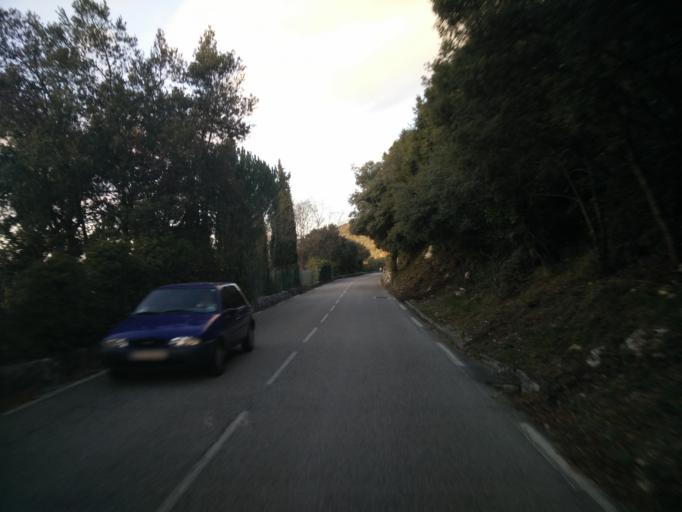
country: FR
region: Provence-Alpes-Cote d'Azur
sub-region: Departement des Alpes-Maritimes
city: La Turbie
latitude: 43.7542
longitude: 7.4036
